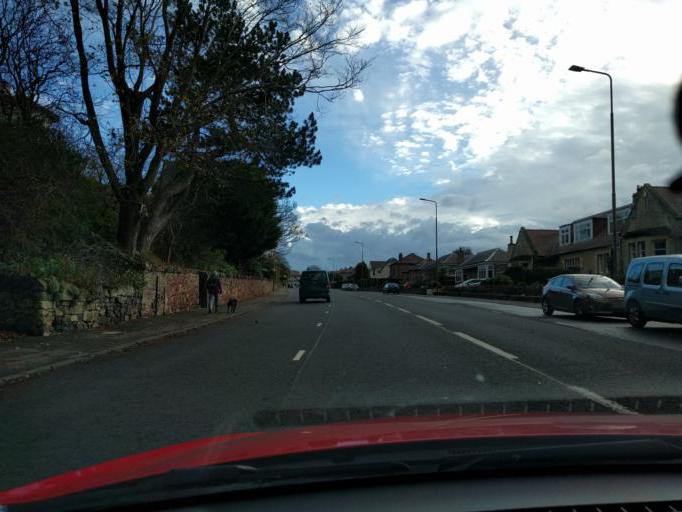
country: GB
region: Scotland
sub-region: Edinburgh
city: Edinburgh
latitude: 55.9121
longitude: -3.2131
